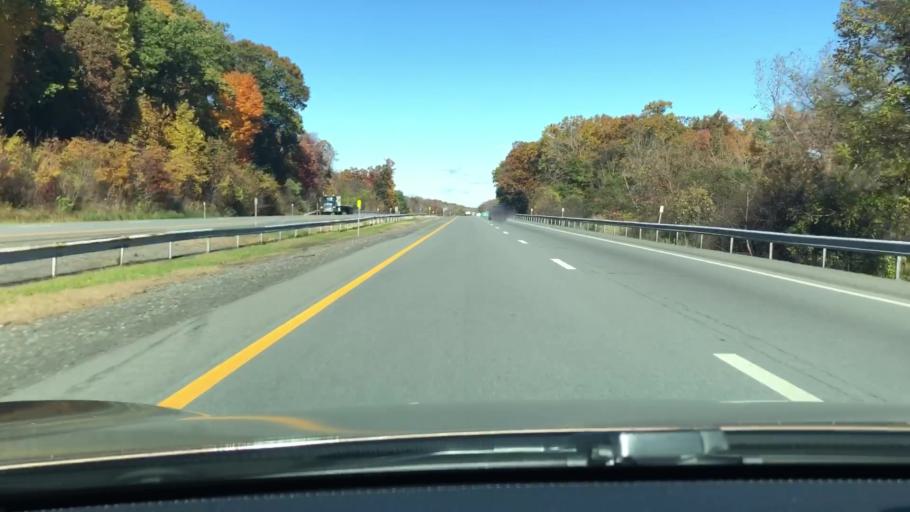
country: US
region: New York
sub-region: Orange County
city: Vails Gate
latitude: 41.4892
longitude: -74.0790
